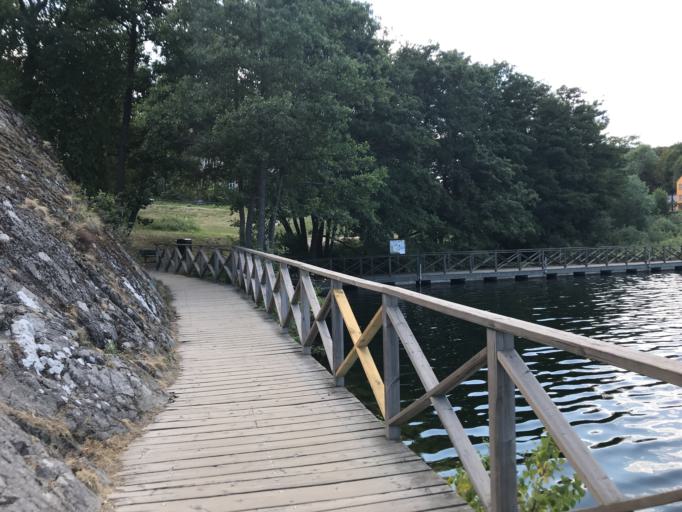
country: SE
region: Stockholm
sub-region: Stockholms Kommun
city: Arsta
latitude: 59.3109
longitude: 18.0111
